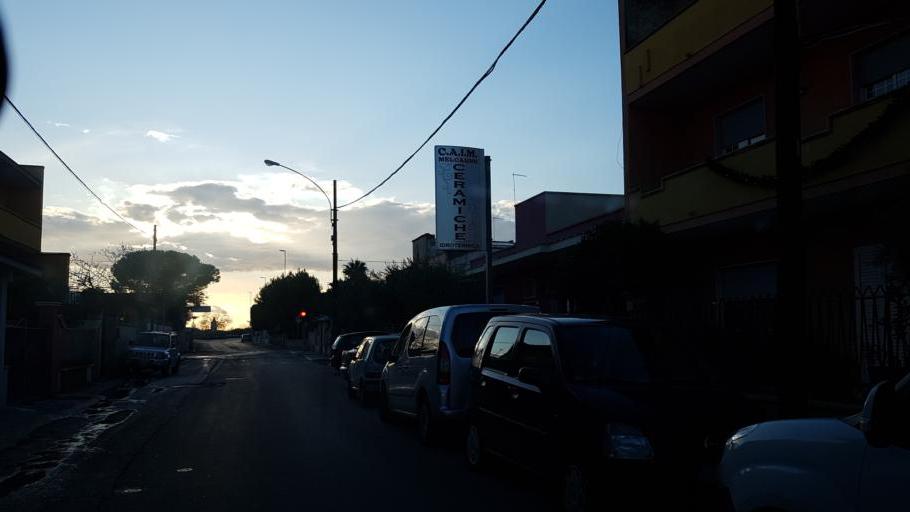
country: IT
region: Apulia
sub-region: Provincia di Lecce
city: Surbo
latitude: 40.3913
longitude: 18.1268
